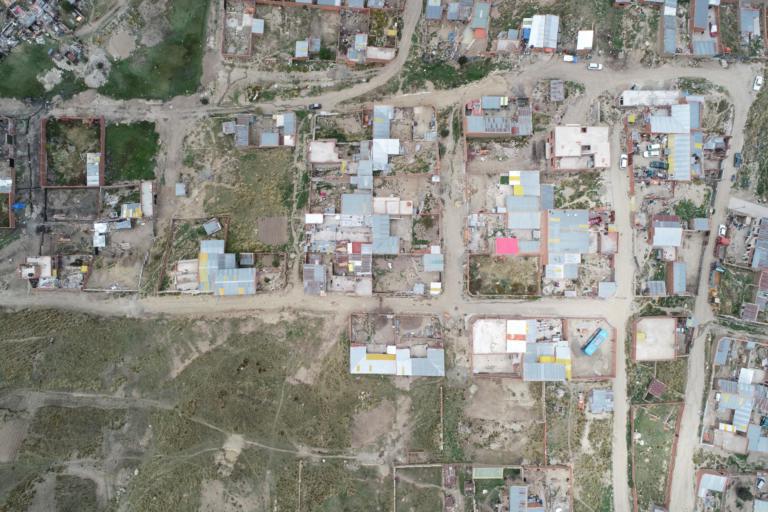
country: BO
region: La Paz
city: La Paz
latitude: -16.4443
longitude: -68.1429
